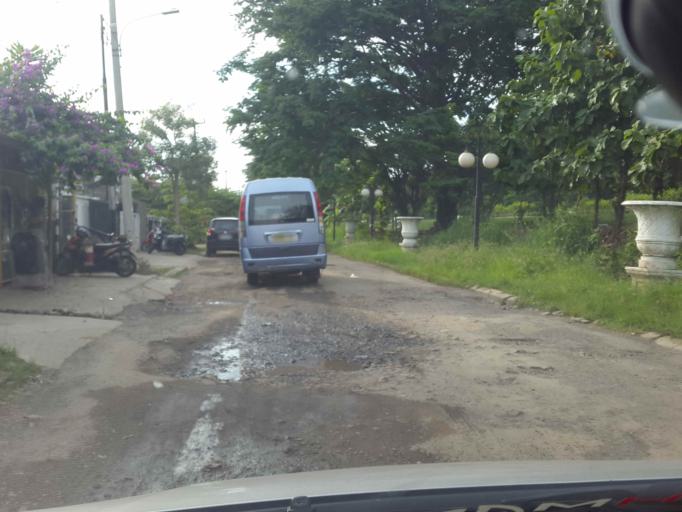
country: ID
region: Banten
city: Pangarengan
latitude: -6.0007
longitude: 106.0608
